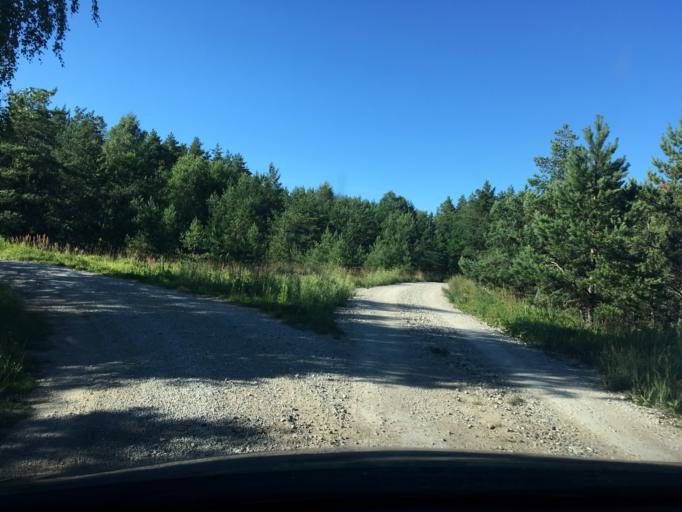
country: EE
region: Laeaene
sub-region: Lihula vald
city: Lihula
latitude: 58.5867
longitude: 23.7469
